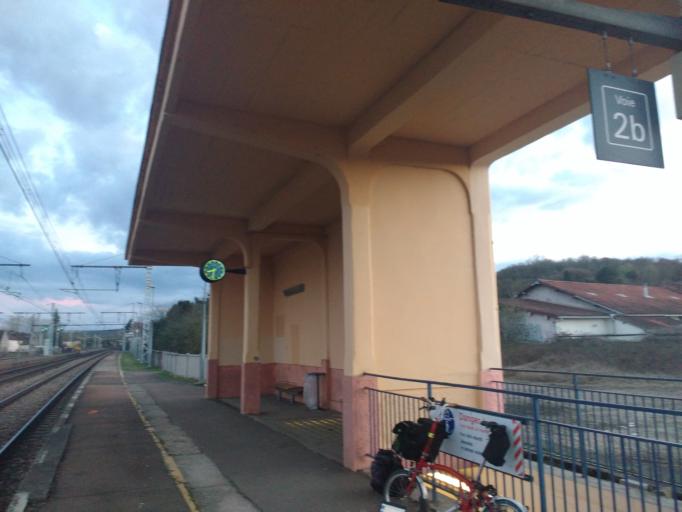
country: FR
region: Bourgogne
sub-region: Departement de l'Yonne
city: Villeneuve-sur-Yonne
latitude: 48.0852
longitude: 3.2865
